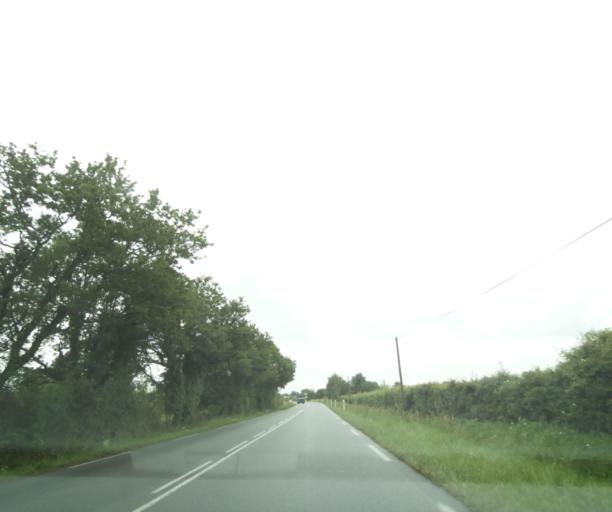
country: FR
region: Poitou-Charentes
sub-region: Departement des Deux-Sevres
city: Viennay
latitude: 46.7024
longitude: -0.2395
